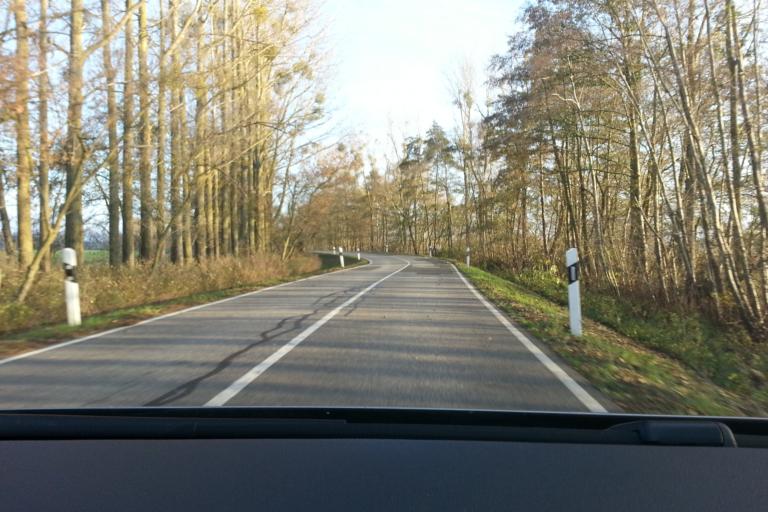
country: DE
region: Mecklenburg-Vorpommern
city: Ducherow
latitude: 53.6520
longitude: 13.7177
